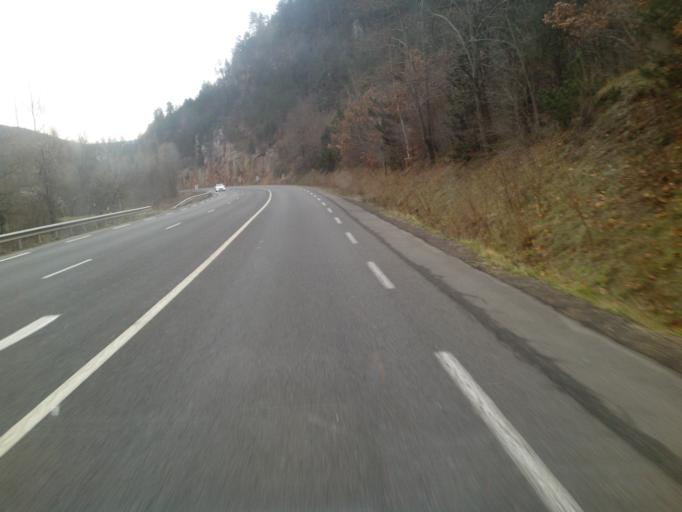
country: FR
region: Languedoc-Roussillon
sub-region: Departement de la Lozere
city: Mende
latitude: 44.4997
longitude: 3.4625
